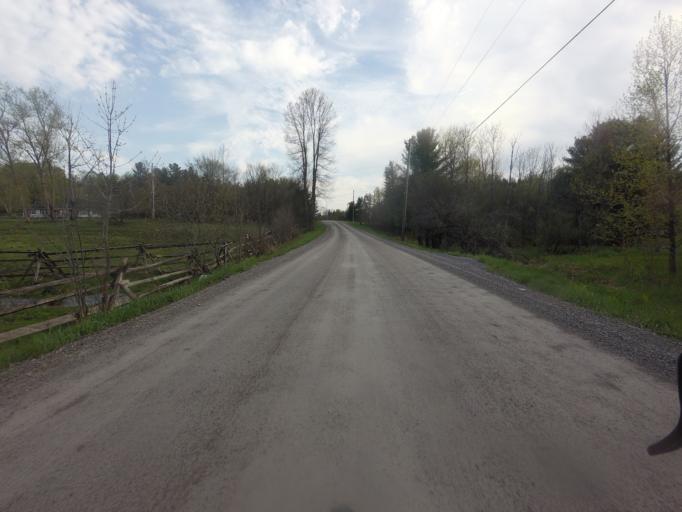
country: CA
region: Ontario
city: Carleton Place
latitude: 45.2047
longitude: -76.3219
